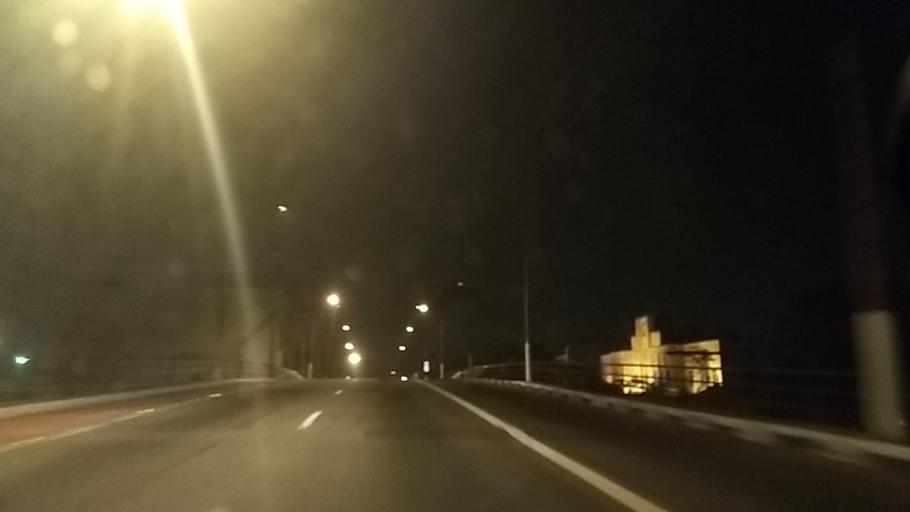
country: BR
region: Sao Paulo
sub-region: Sao Paulo
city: Sao Paulo
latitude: -23.5439
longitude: -46.6182
